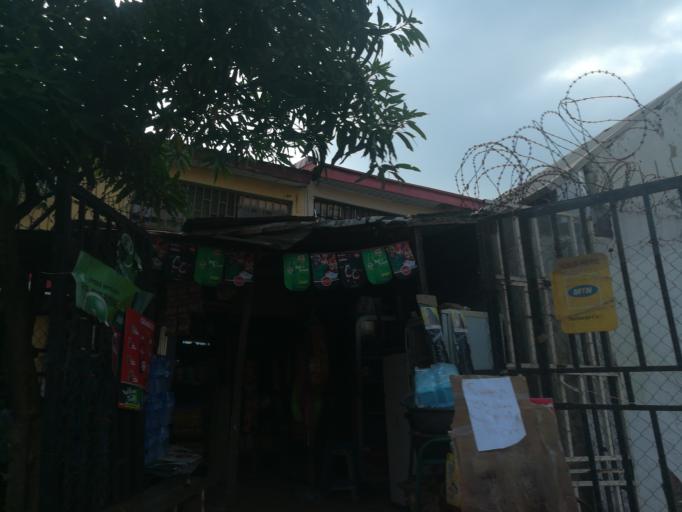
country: NG
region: Abuja Federal Capital Territory
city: Abuja
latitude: 9.0803
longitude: 7.4139
